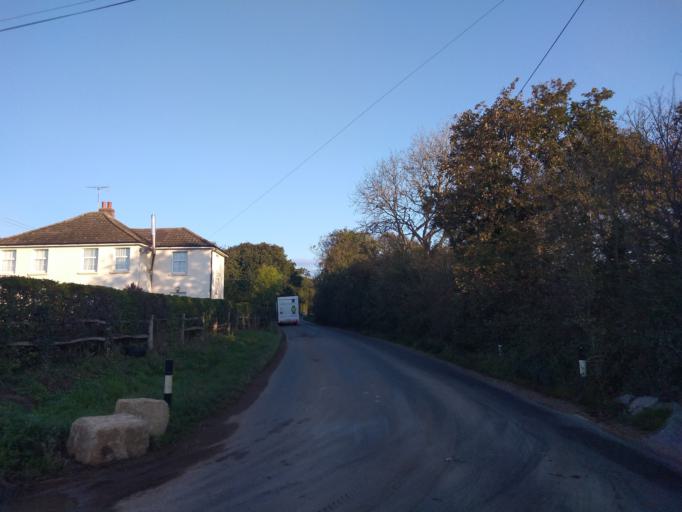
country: GB
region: England
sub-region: West Sussex
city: Goring-by-Sea
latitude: 50.8278
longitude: -0.4344
